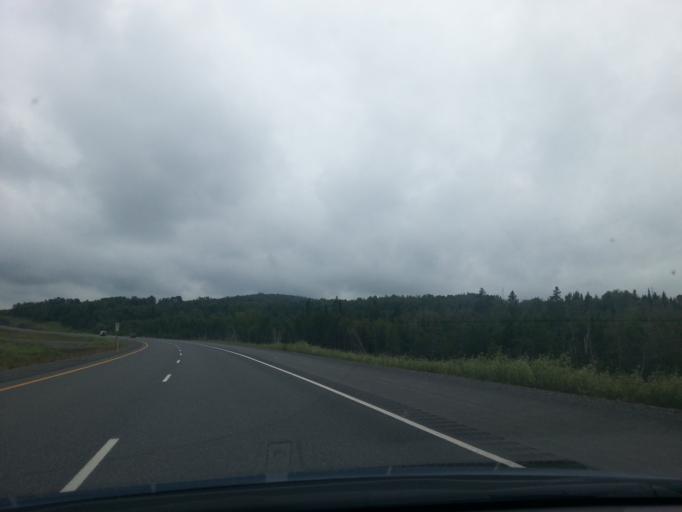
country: CA
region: New Brunswick
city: Florenceville-Bristol
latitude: 46.5065
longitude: -67.6972
